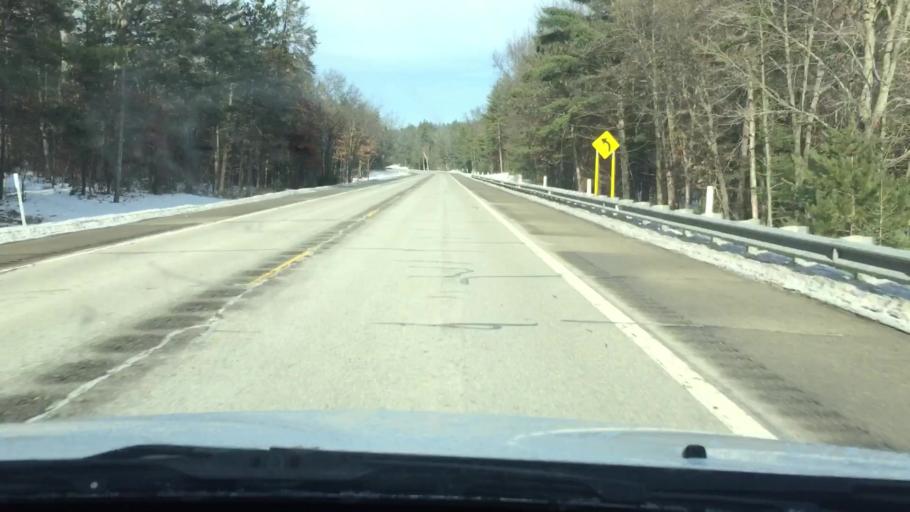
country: US
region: Michigan
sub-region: Wexford County
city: Manton
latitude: 44.5421
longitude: -85.3740
